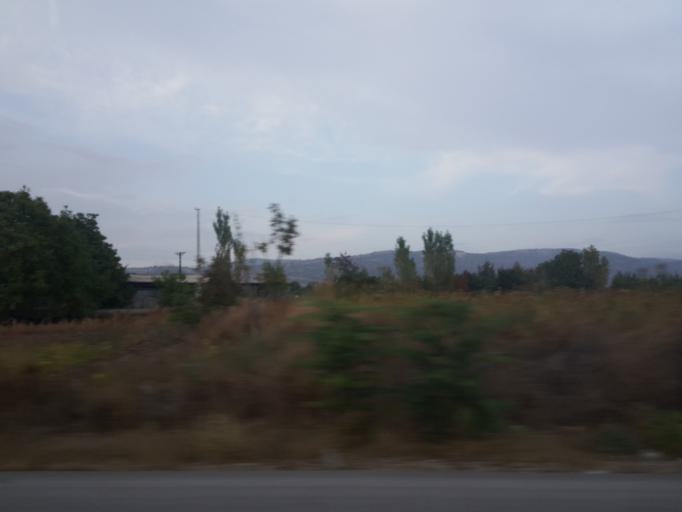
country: TR
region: Amasya
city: Gumushacikoy
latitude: 40.8771
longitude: 35.2320
